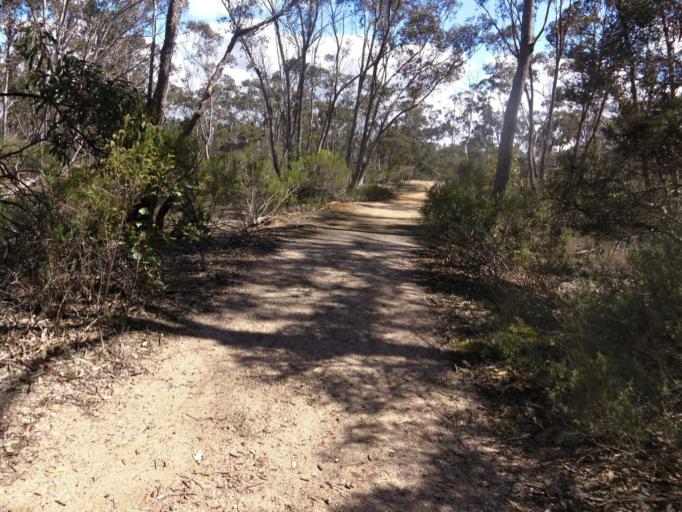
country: AU
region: Victoria
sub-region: Melton
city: Melton West
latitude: -37.6611
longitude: 144.5073
